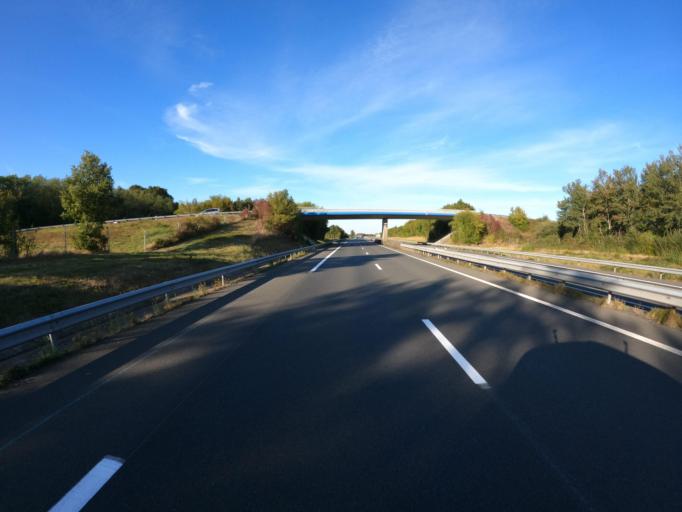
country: FR
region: Pays de la Loire
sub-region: Departement de Maine-et-Loire
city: Chemille-Melay
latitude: 47.2004
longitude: -0.7719
